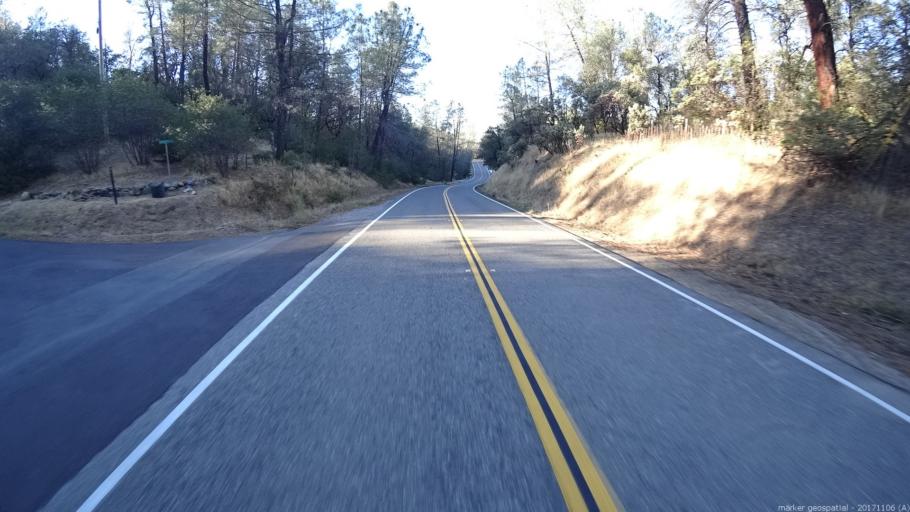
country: US
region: California
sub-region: Shasta County
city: Shasta
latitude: 40.5694
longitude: -122.4732
